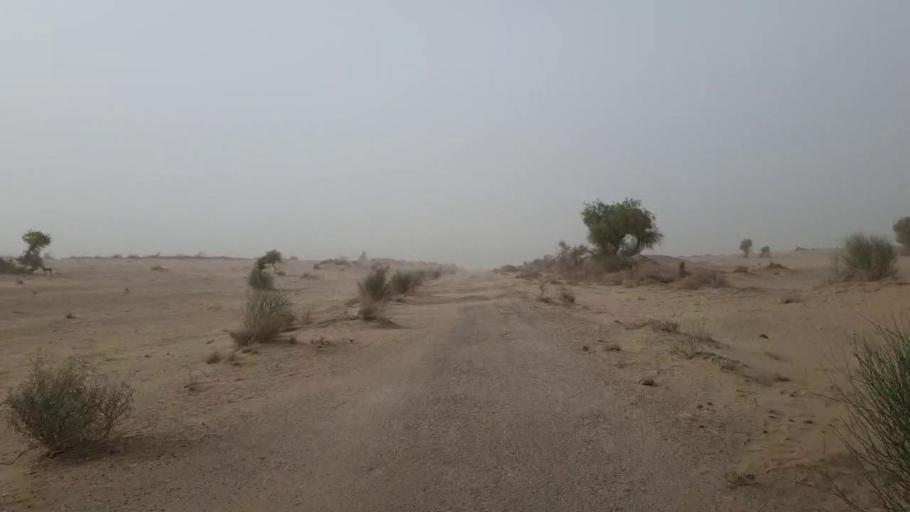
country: PK
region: Sindh
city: Islamkot
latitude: 24.5649
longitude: 70.3627
